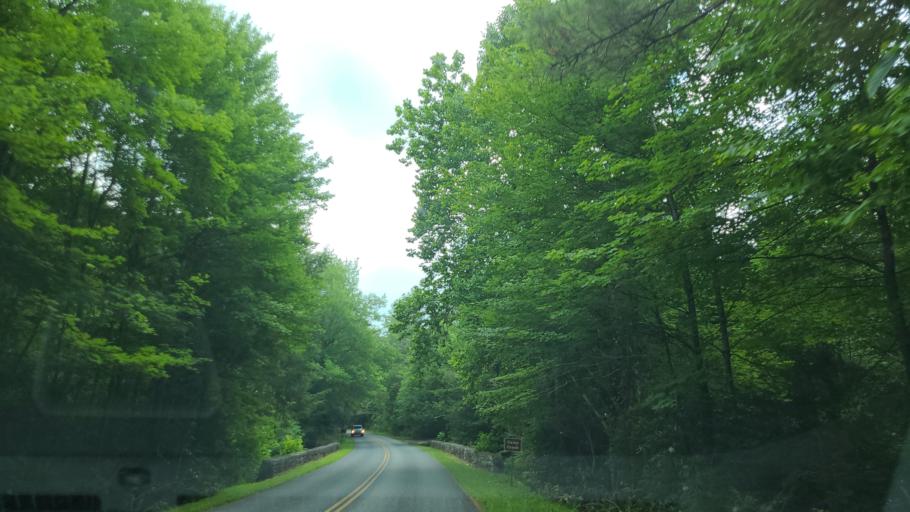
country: US
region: North Carolina
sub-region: Avery County
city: Newland
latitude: 35.9787
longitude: -81.9200
